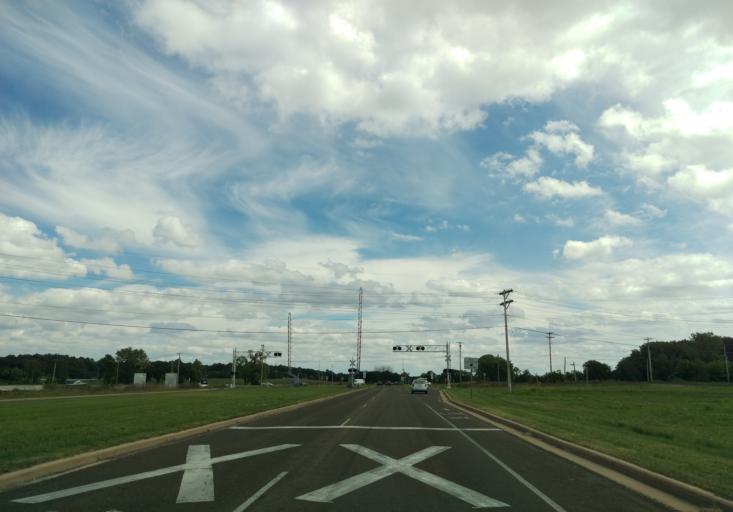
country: US
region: Wisconsin
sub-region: Dane County
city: Maple Bluff
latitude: 43.1533
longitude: -89.4072
